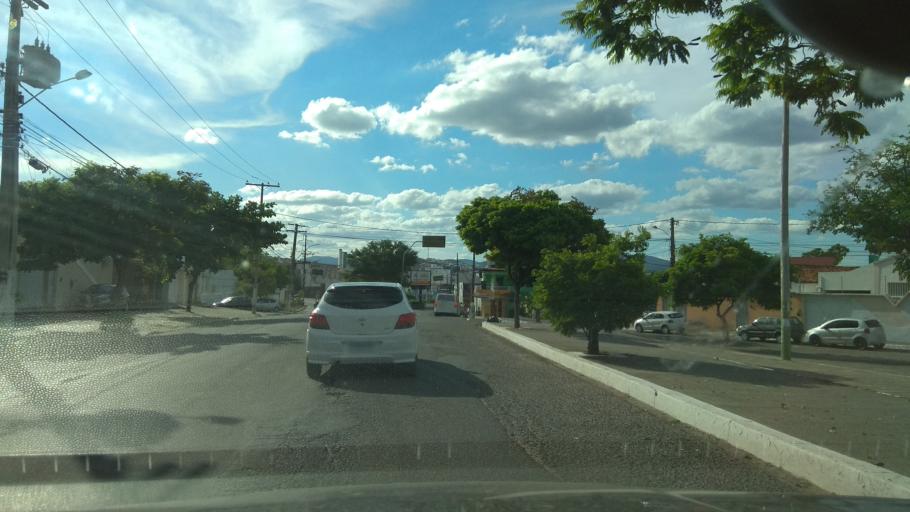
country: BR
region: Bahia
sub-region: Jequie
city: Jequie
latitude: -13.8671
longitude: -40.0765
